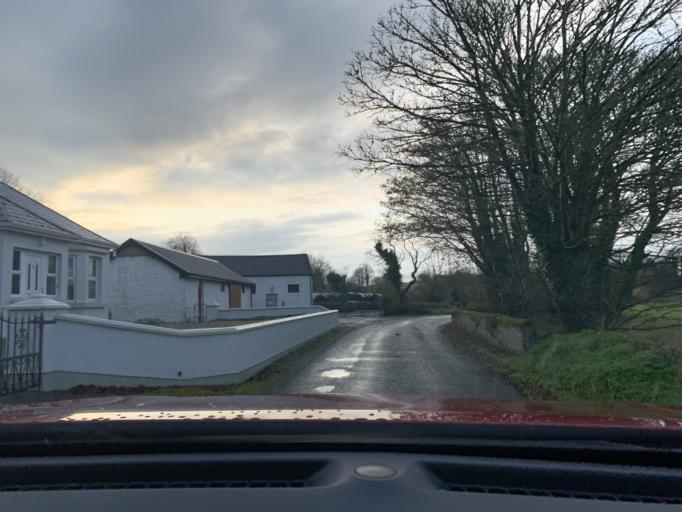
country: IE
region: Connaught
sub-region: Sligo
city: Ballymote
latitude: 54.0416
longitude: -8.5514
